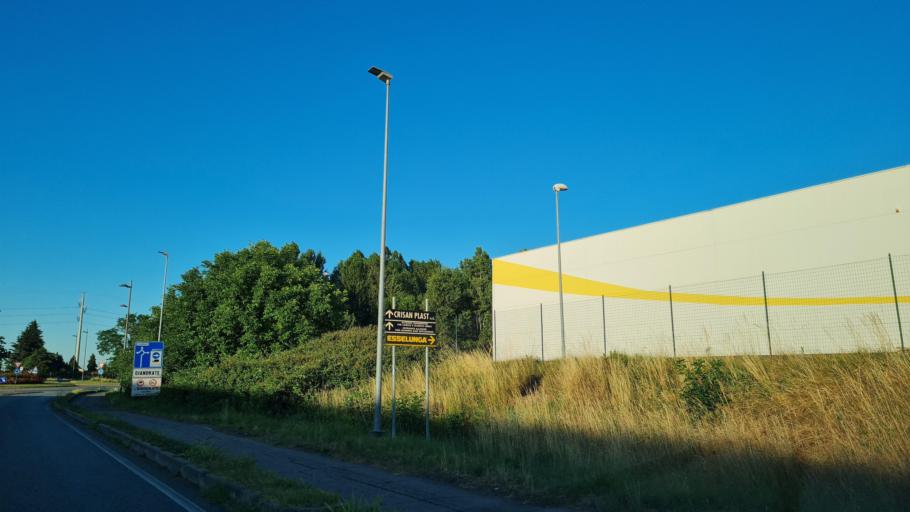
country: IT
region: Piedmont
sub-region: Provincia di Novara
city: Biandrate
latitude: 45.4605
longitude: 8.4643
